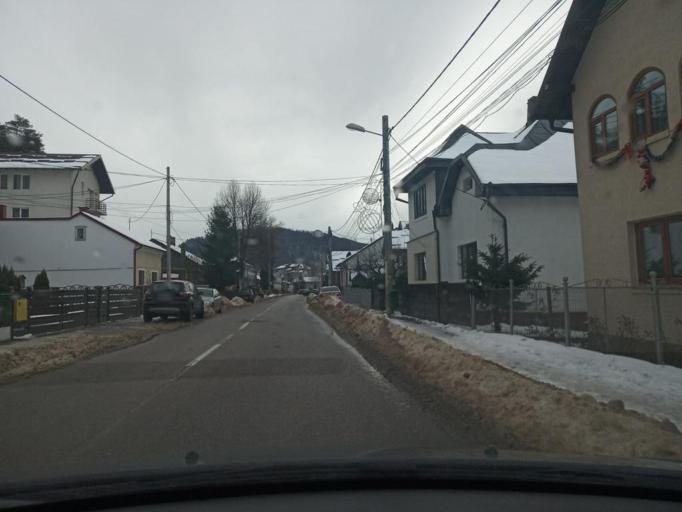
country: RO
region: Suceava
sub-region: Oras Gura Humorului
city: Gura Humorului
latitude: 47.5585
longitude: 25.8892
